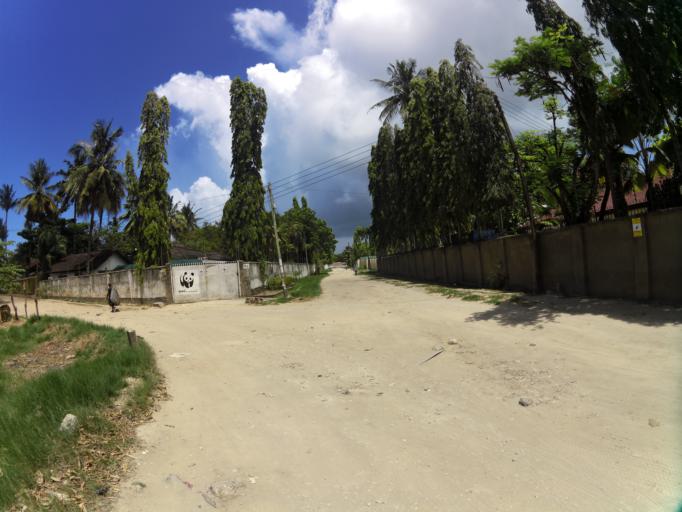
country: TZ
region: Dar es Salaam
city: Magomeni
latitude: -6.7724
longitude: 39.2542
